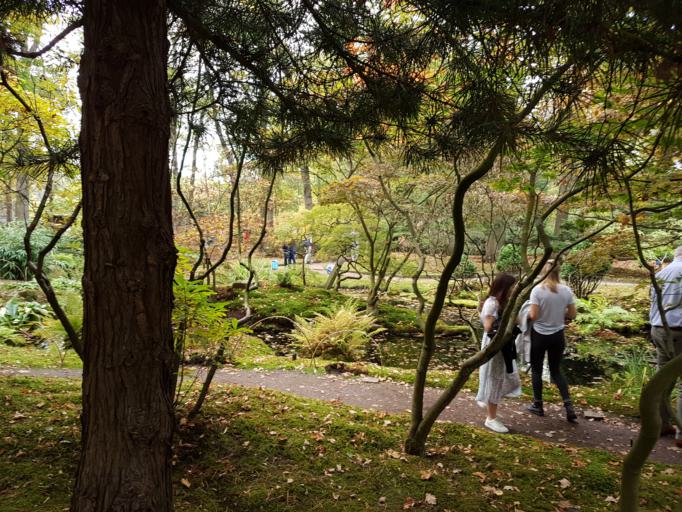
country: NL
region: South Holland
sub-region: Gemeente Leidschendam-Voorburg
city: Voorburg
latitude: 52.1001
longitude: 4.3335
